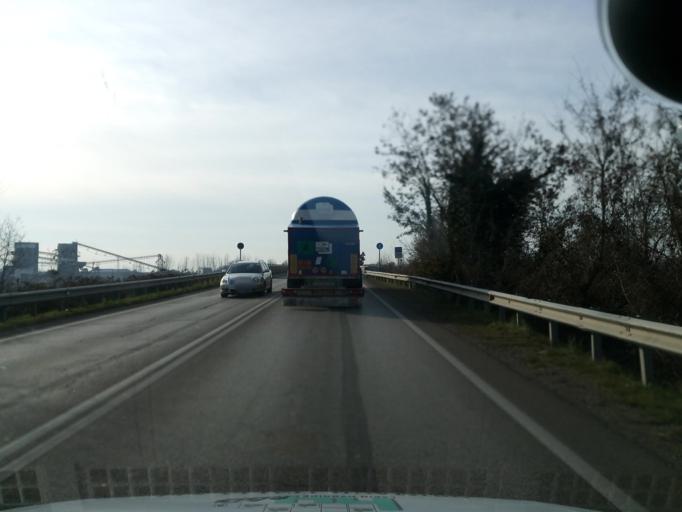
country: IT
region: Veneto
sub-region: Provincia di Vicenza
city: Sandrigo
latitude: 45.6517
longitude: 11.5815
